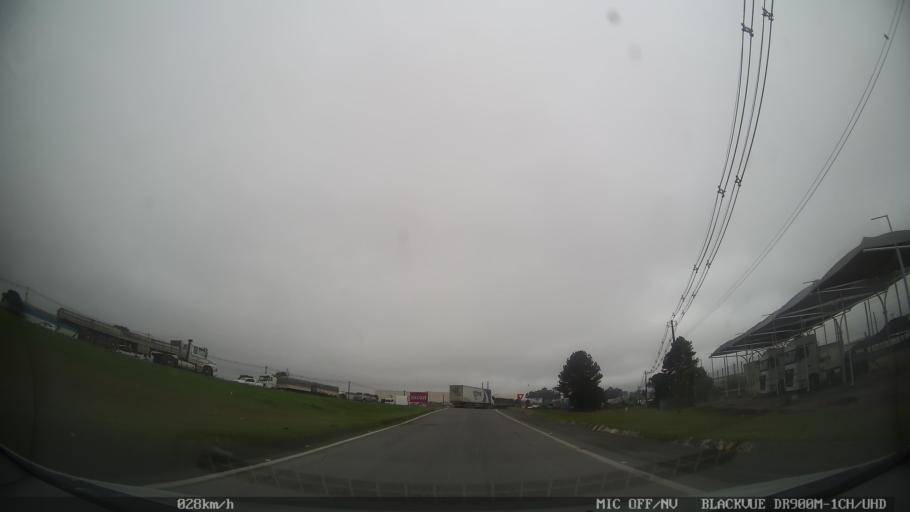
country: BR
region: Parana
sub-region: Sao Jose Dos Pinhais
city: Sao Jose dos Pinhais
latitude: -25.5681
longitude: -49.1728
